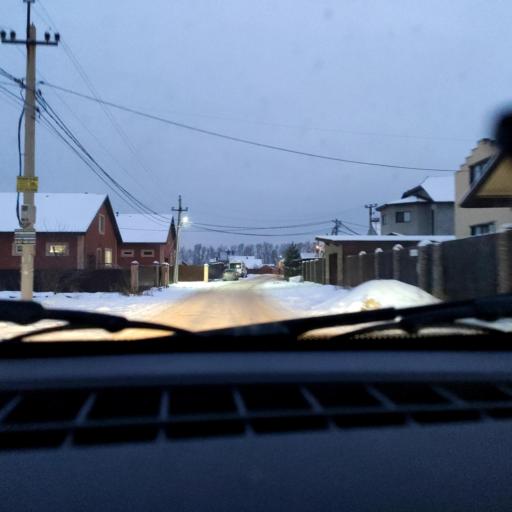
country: RU
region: Bashkortostan
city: Ufa
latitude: 54.6774
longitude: 56.0906
